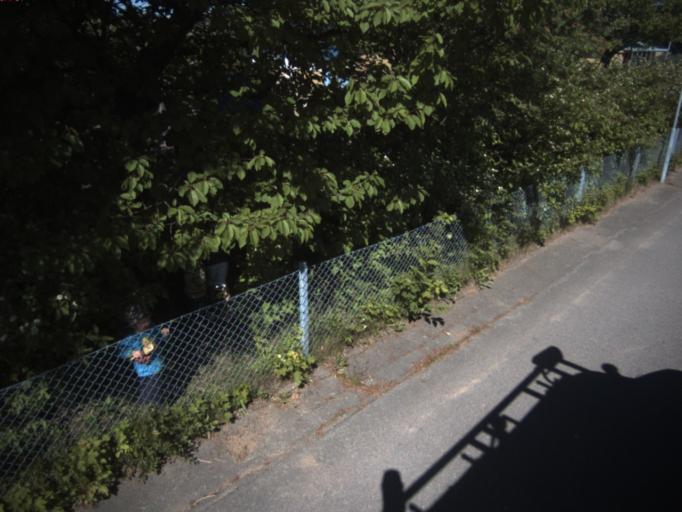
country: SE
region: Skane
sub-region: Helsingborg
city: Rydeback
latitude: 55.9614
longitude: 12.7688
